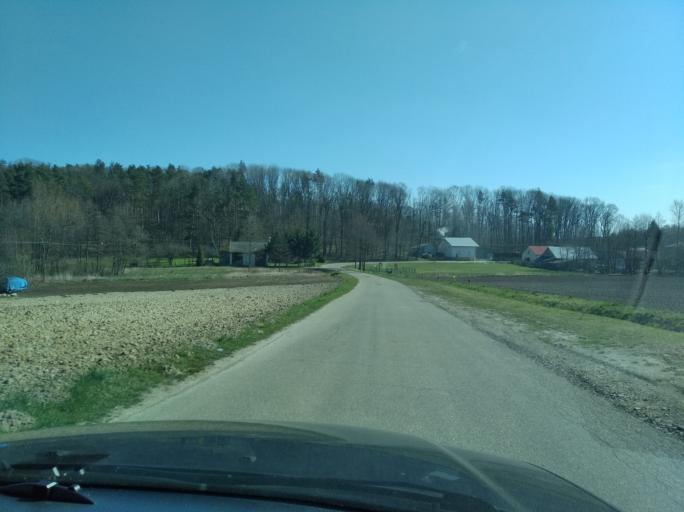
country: PL
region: Subcarpathian Voivodeship
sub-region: Powiat jaroslawski
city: Pawlosiow
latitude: 49.9610
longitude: 22.6665
